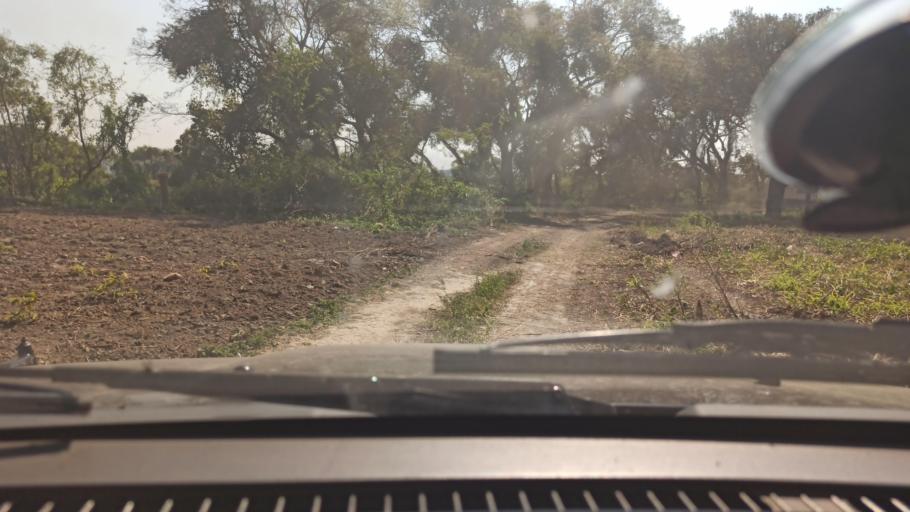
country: PY
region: Asuncion
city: Asuncion
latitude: -25.3502
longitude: -57.6709
